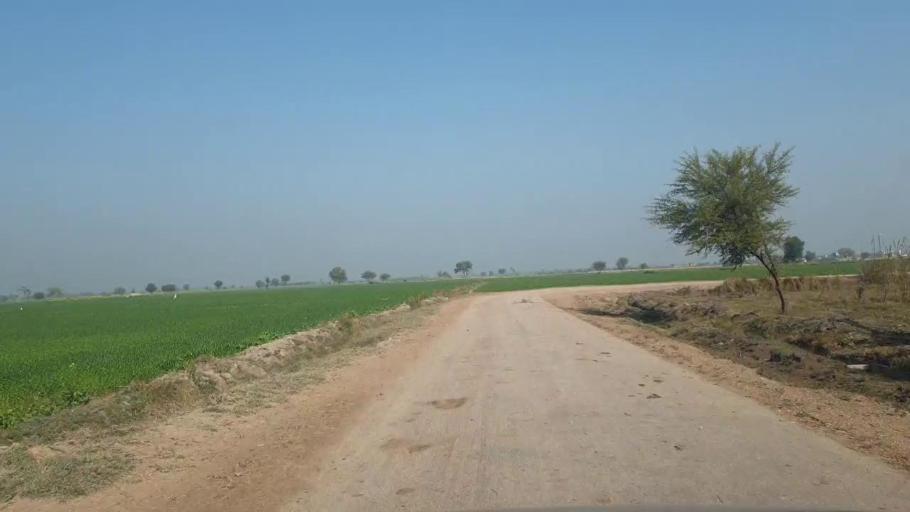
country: PK
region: Sindh
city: Shahdadpur
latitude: 25.9753
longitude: 68.5876
